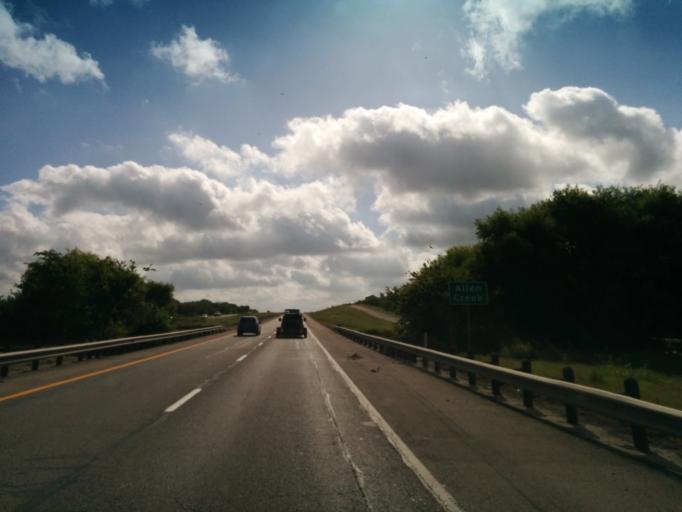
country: US
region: Texas
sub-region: Caldwell County
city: Luling
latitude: 29.6328
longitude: -97.7420
